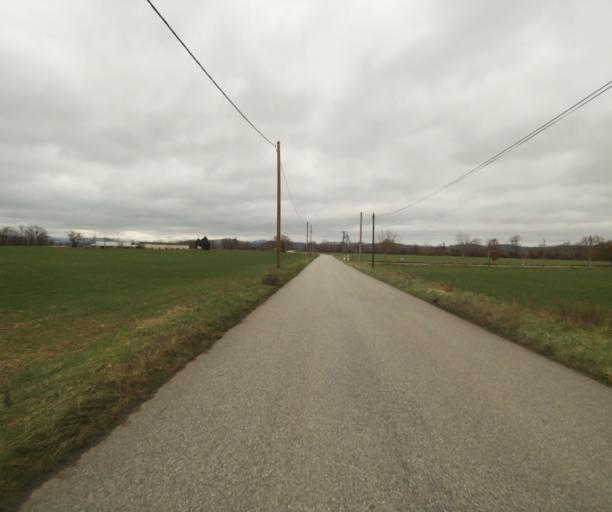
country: FR
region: Midi-Pyrenees
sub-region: Departement de l'Ariege
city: Pamiers
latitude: 43.1443
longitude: 1.6340
